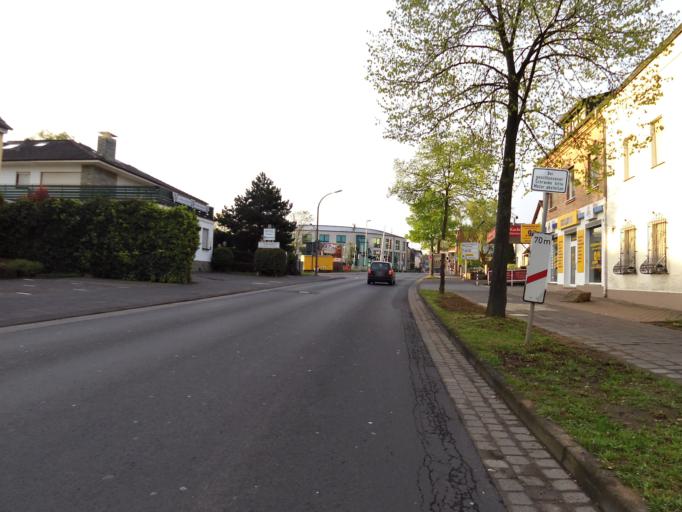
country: DE
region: North Rhine-Westphalia
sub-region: Regierungsbezirk Koln
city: Rheinbach
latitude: 50.6295
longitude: 6.9440
